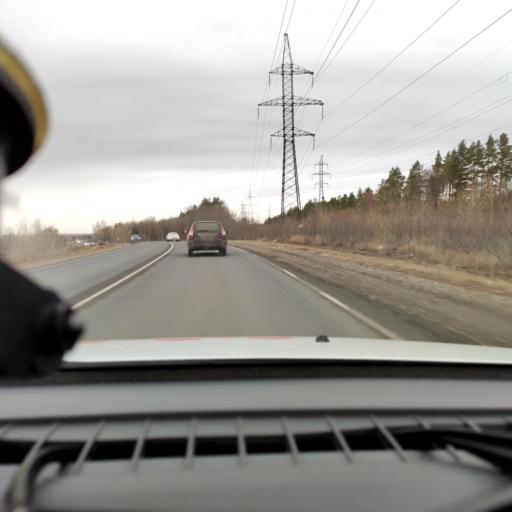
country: RU
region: Samara
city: Samara
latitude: 53.1242
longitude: 50.2039
